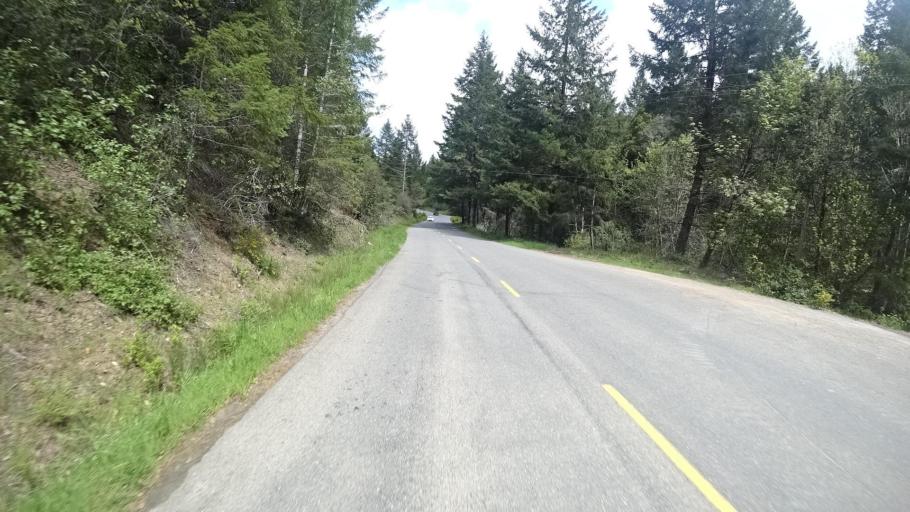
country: US
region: California
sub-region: Humboldt County
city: Redway
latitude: 40.0933
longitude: -123.9314
